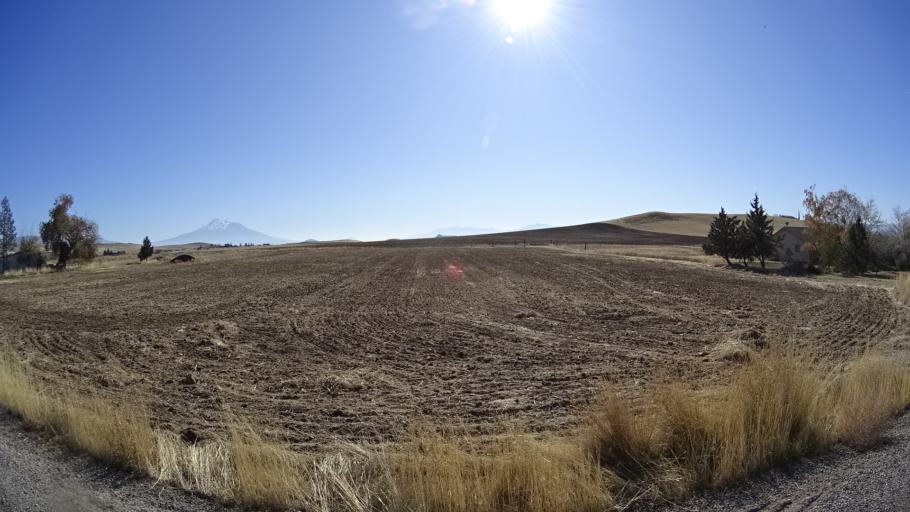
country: US
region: California
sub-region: Siskiyou County
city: Montague
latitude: 41.7558
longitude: -122.4647
